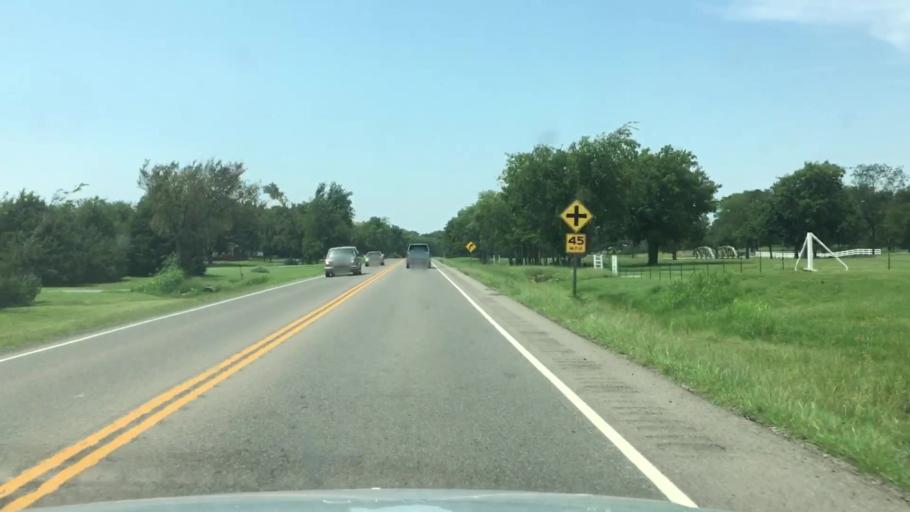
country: US
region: Oklahoma
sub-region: Wagoner County
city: Wagoner
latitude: 35.9380
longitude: -95.3119
